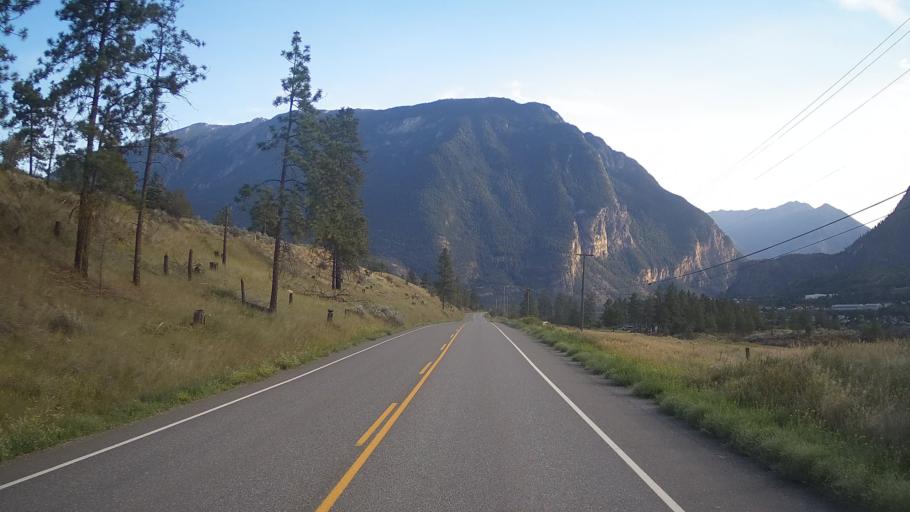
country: CA
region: British Columbia
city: Lillooet
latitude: 50.6982
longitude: -121.9165
